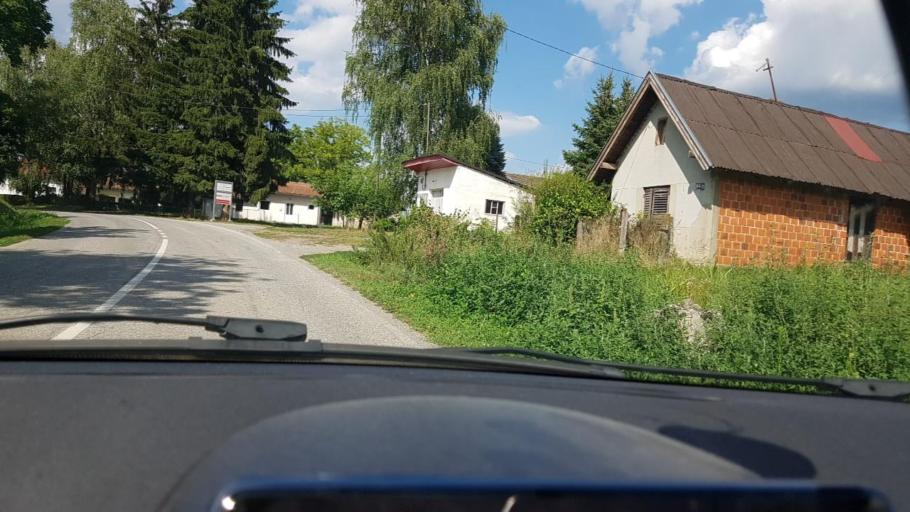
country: HR
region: Bjelovarsko-Bilogorska
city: Zdralovi
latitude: 45.8442
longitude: 16.9732
